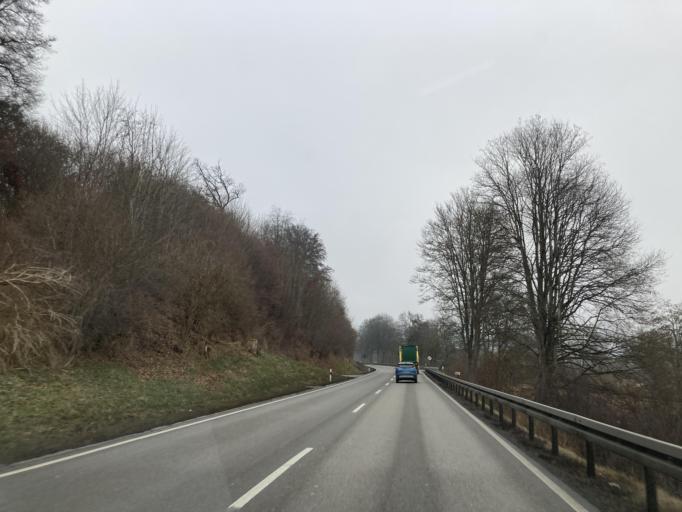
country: DE
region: Baden-Wuerttemberg
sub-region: Freiburg Region
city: Immendingen
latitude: 47.9407
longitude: 8.7605
